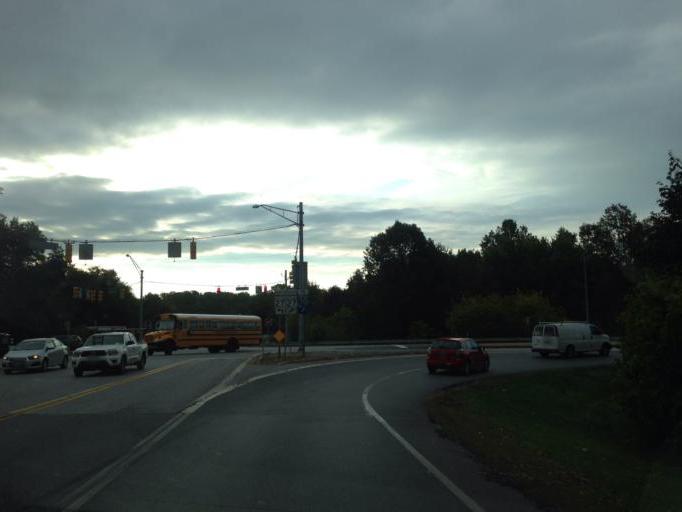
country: US
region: Maryland
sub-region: Carroll County
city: Mount Airy
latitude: 39.3623
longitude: -77.1645
